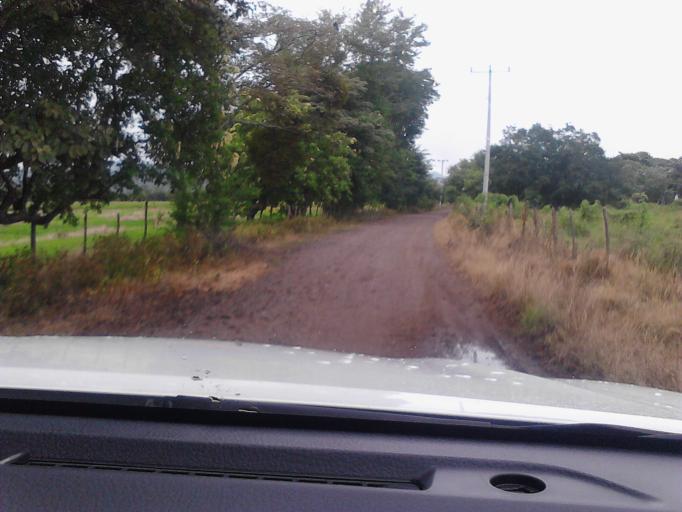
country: NI
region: Matagalpa
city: Ciudad Dario
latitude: 12.9001
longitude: -86.1427
